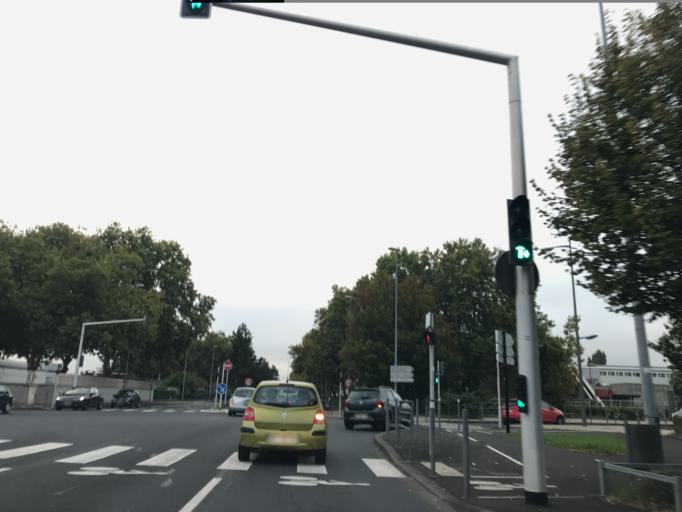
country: FR
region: Auvergne
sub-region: Departement du Puy-de-Dome
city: Gerzat
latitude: 45.7999
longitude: 3.1214
